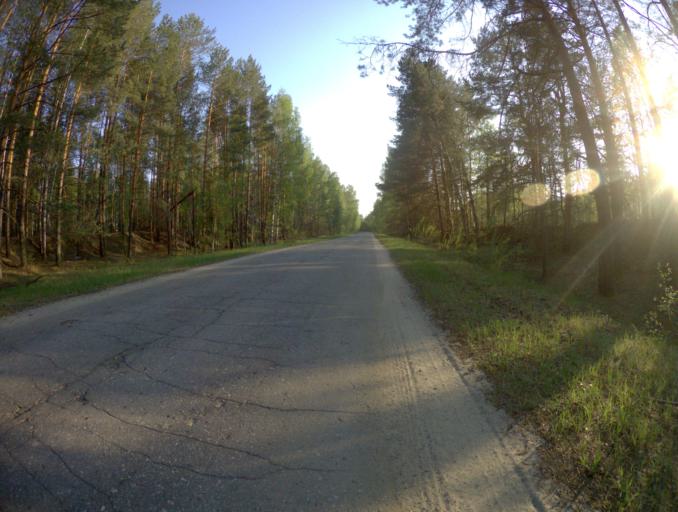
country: RU
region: Vladimir
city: Vyazniki
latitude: 56.3327
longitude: 42.1272
